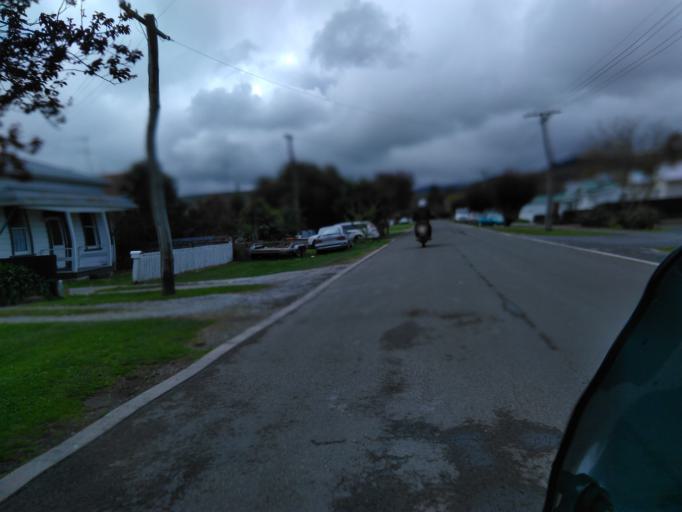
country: NZ
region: Gisborne
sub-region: Gisborne District
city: Gisborne
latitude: -38.6533
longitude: 178.0081
